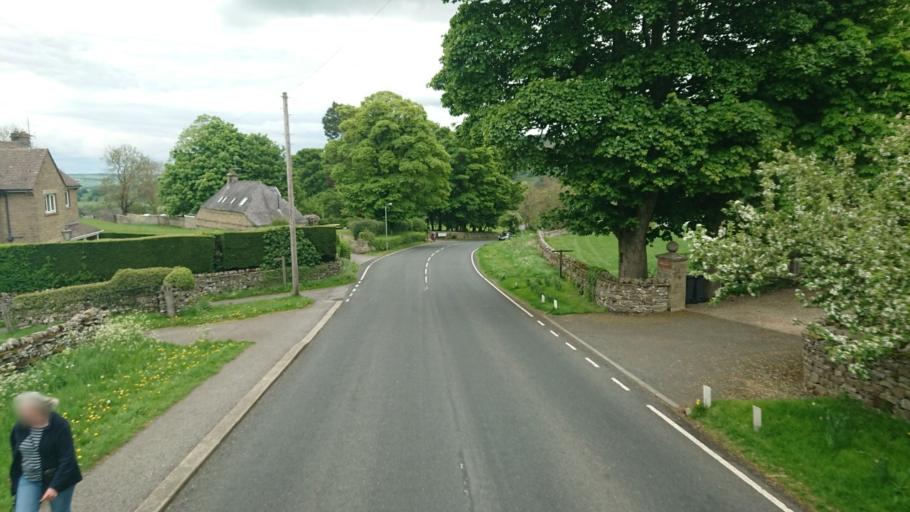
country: GB
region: England
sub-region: North Yorkshire
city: Leyburn
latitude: 54.2906
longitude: -1.9818
